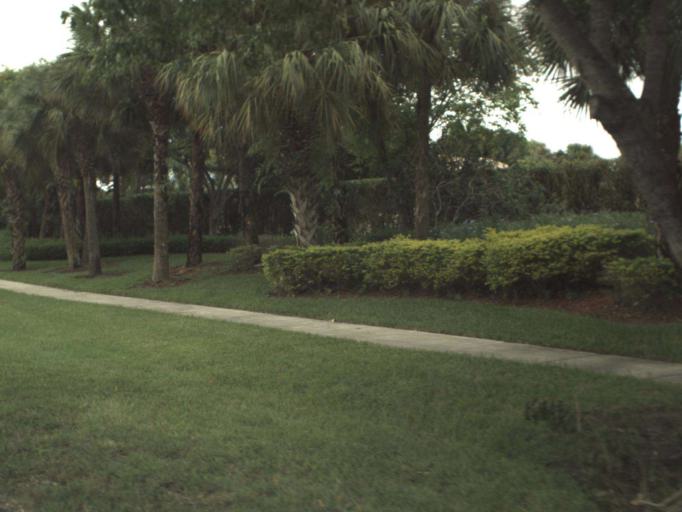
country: US
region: Florida
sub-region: Broward County
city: Coral Springs
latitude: 26.2334
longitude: -80.2882
